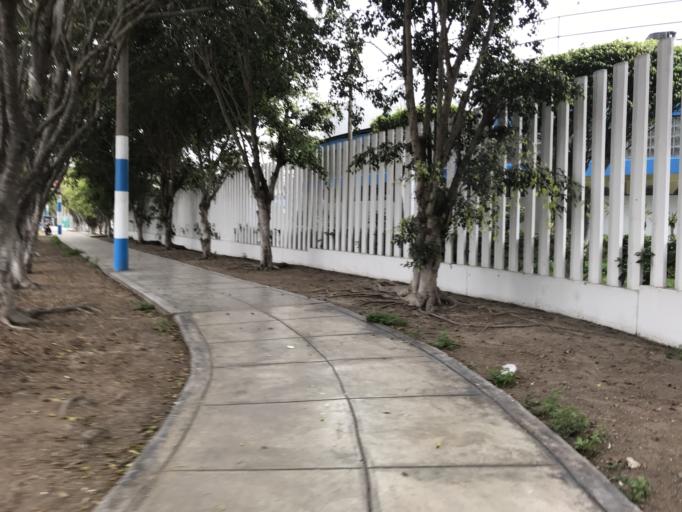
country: PE
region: Lima
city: Lima
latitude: -12.0773
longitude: -77.0381
